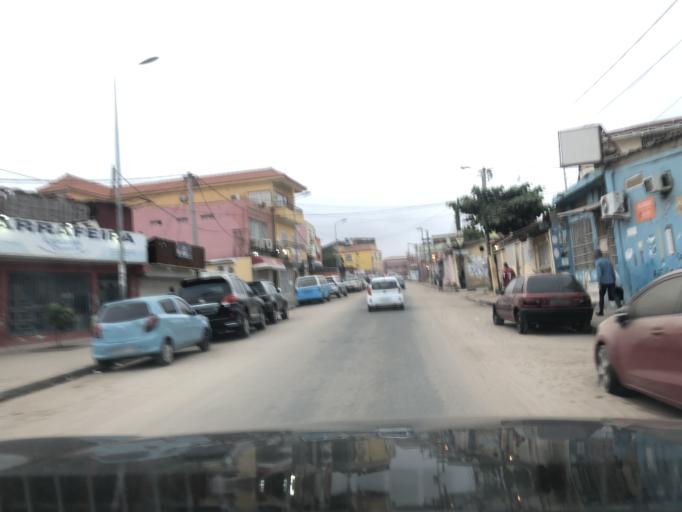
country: AO
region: Luanda
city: Luanda
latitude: -8.8455
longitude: 13.2251
